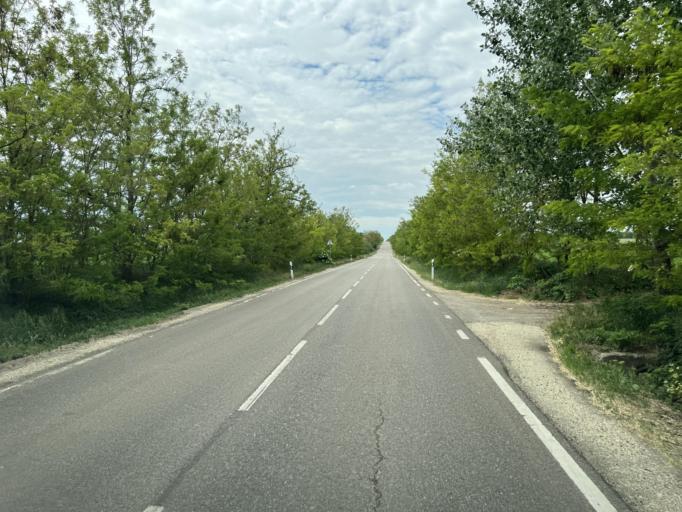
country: HU
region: Pest
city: Zsambok
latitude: 47.5344
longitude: 19.6043
